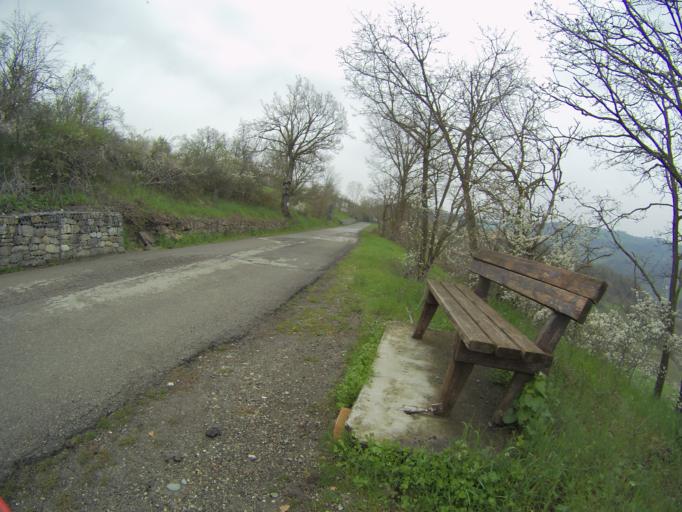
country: IT
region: Emilia-Romagna
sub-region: Provincia di Reggio Emilia
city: Casina
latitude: 44.5356
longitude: 10.4608
